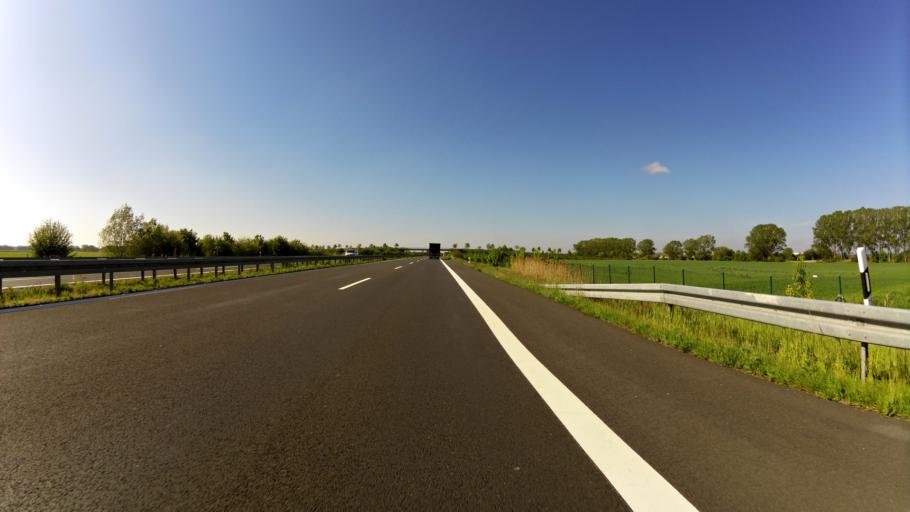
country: DE
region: Brandenburg
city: Trebbin
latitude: 52.1802
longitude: 13.2478
